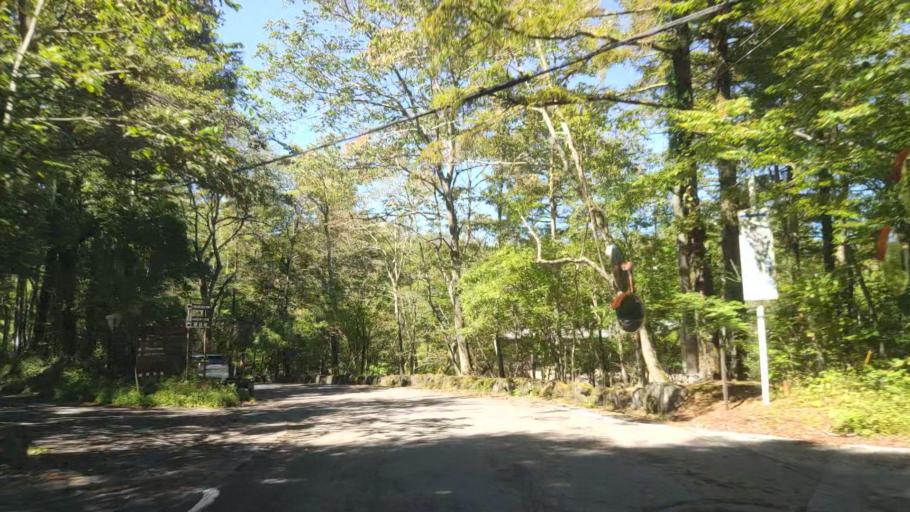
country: JP
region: Shizuoka
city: Gotemba
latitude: 35.4059
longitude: 138.8585
